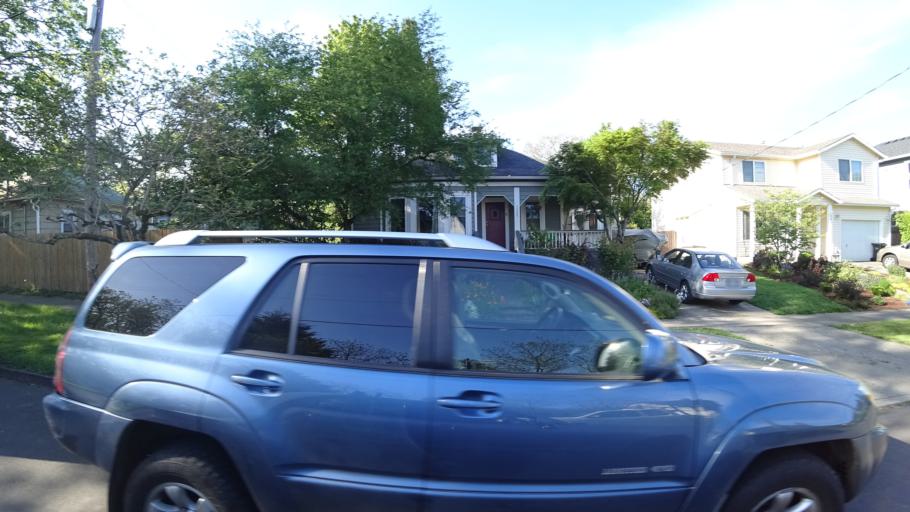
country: US
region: Oregon
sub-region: Clackamas County
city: Milwaukie
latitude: 45.4600
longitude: -122.6446
